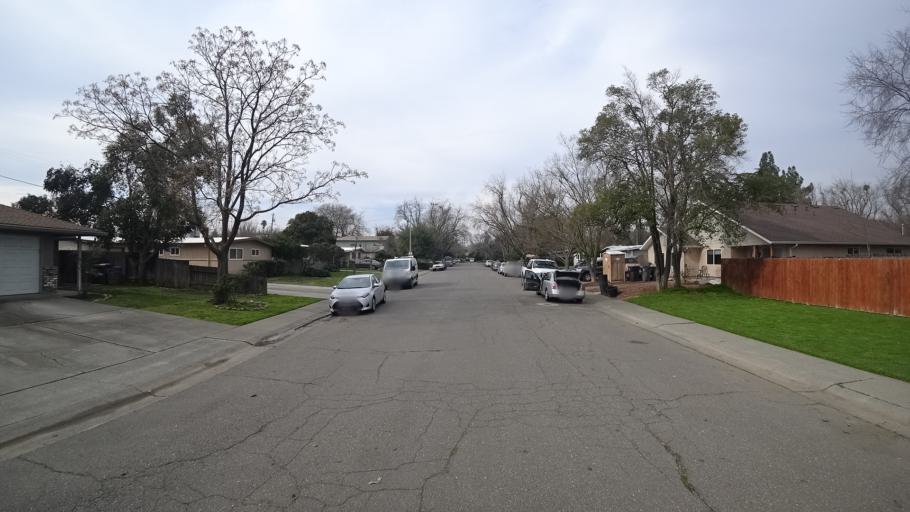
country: US
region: California
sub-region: Yolo County
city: Davis
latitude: 38.5501
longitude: -121.7291
